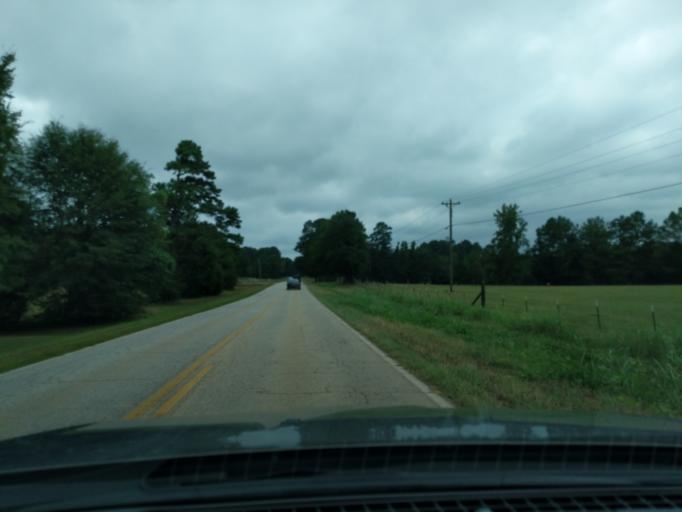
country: US
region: Georgia
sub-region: Columbia County
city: Appling
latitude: 33.6306
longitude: -82.3997
